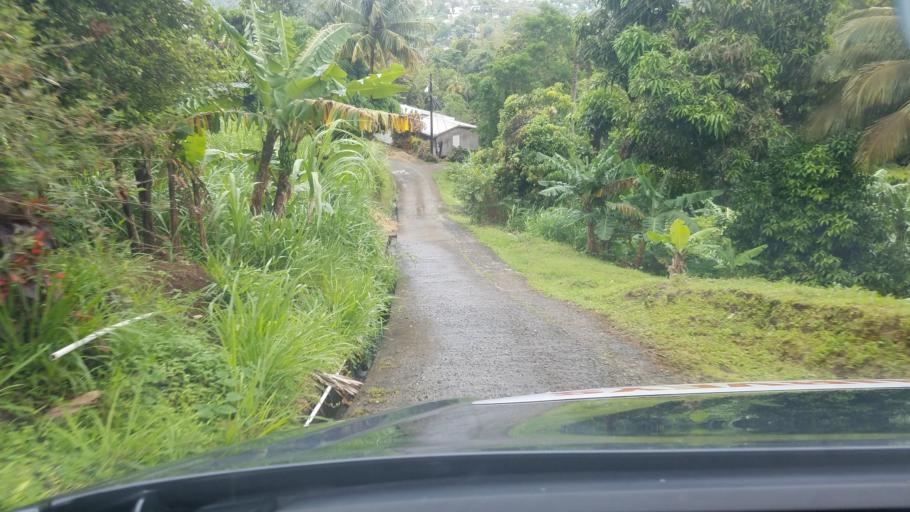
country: LC
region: Castries Quarter
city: Bisee
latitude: 13.9945
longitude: -60.9726
